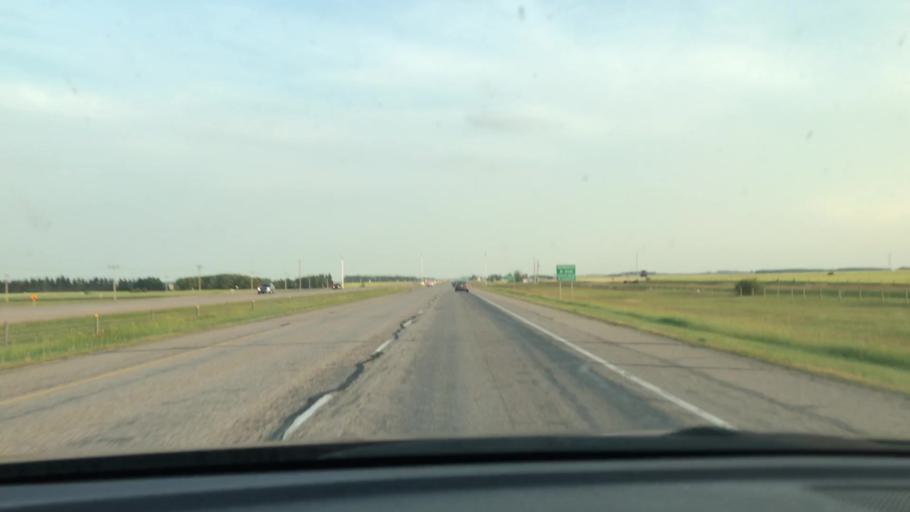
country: CA
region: Alberta
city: Olds
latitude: 51.8562
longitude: -114.0257
